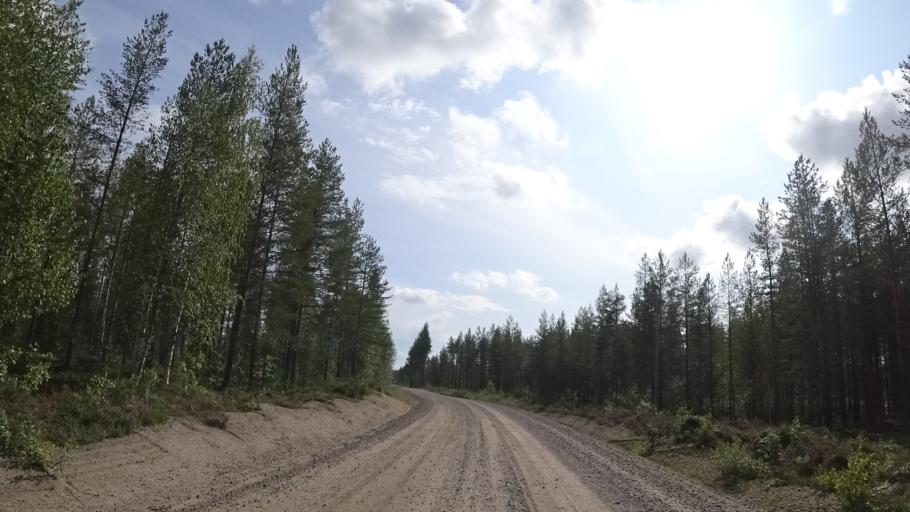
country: FI
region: North Karelia
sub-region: Pielisen Karjala
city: Lieksa
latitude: 63.5541
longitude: 30.0620
